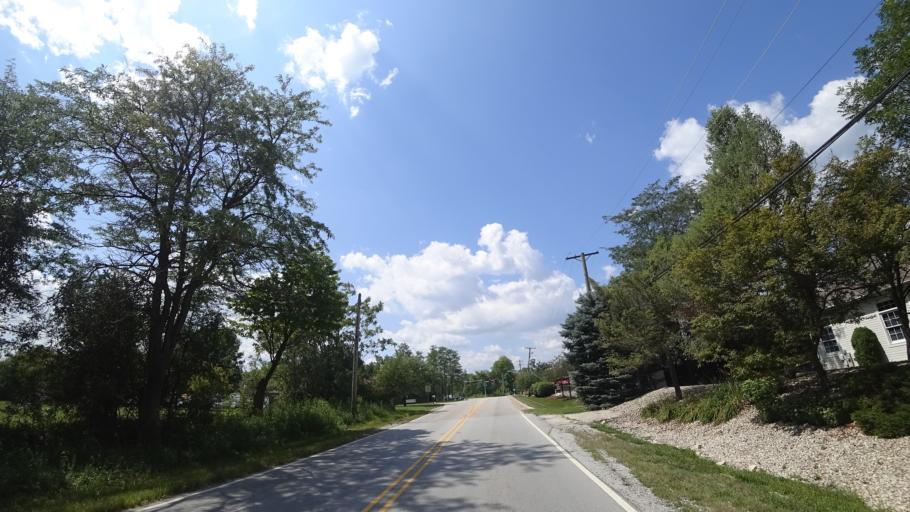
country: US
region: Illinois
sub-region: Cook County
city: Oak Forest
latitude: 41.6244
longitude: -87.7833
